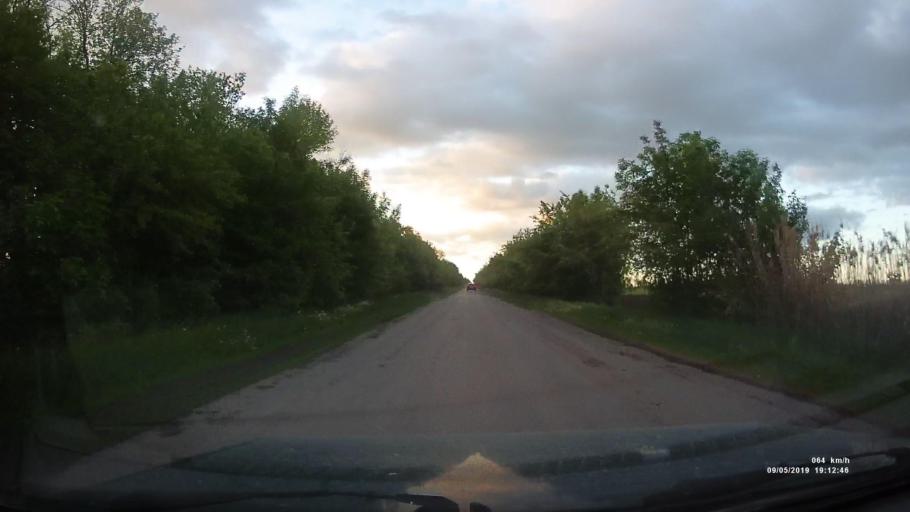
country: RU
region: Krasnodarskiy
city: Kanelovskaya
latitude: 46.7445
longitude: 39.2137
